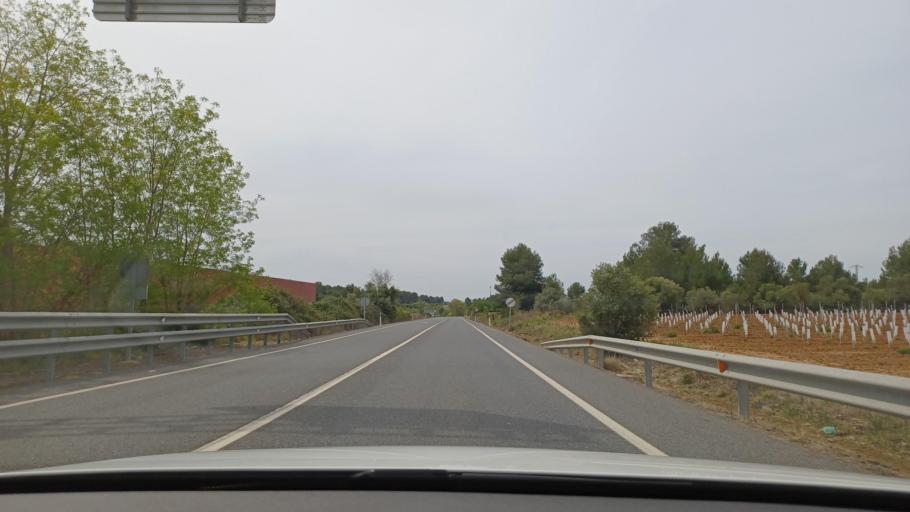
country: ES
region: Catalonia
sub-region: Provincia de Tarragona
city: la Pobla de Mafumet
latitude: 41.1843
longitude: 1.2417
